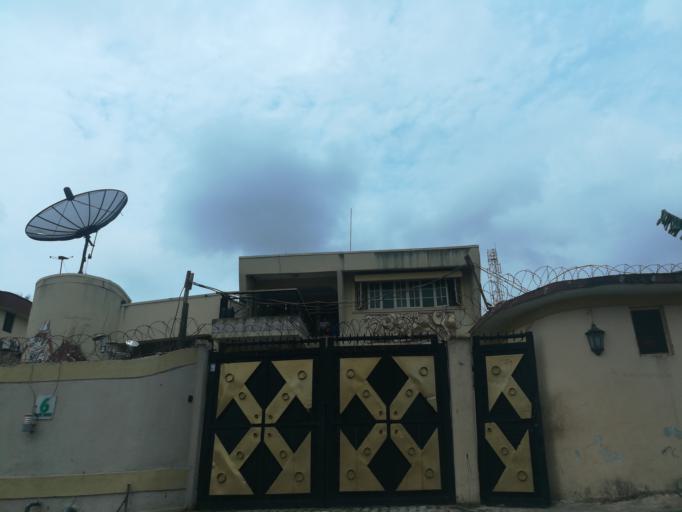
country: NG
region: Lagos
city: Ojota
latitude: 6.5894
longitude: 3.3664
